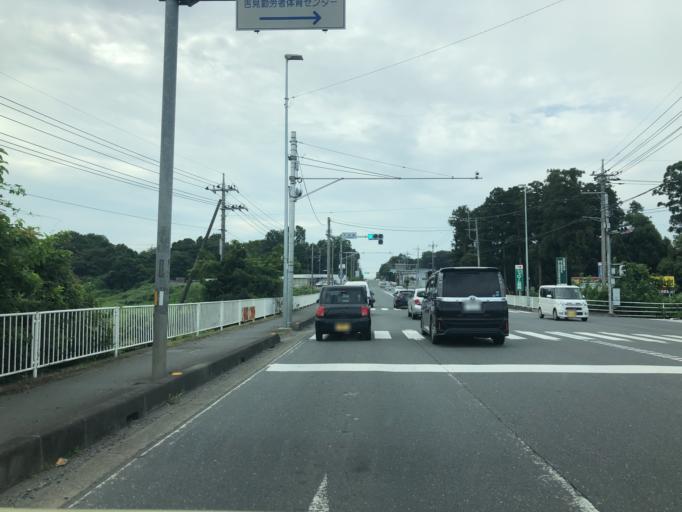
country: JP
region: Saitama
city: Fukiage-fujimi
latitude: 36.0456
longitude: 139.4137
